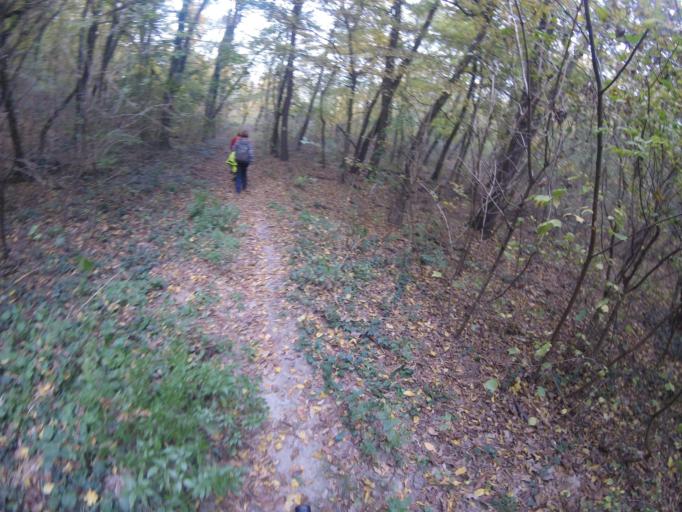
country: HU
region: Fejer
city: Bodajk
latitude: 47.3172
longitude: 18.2124
